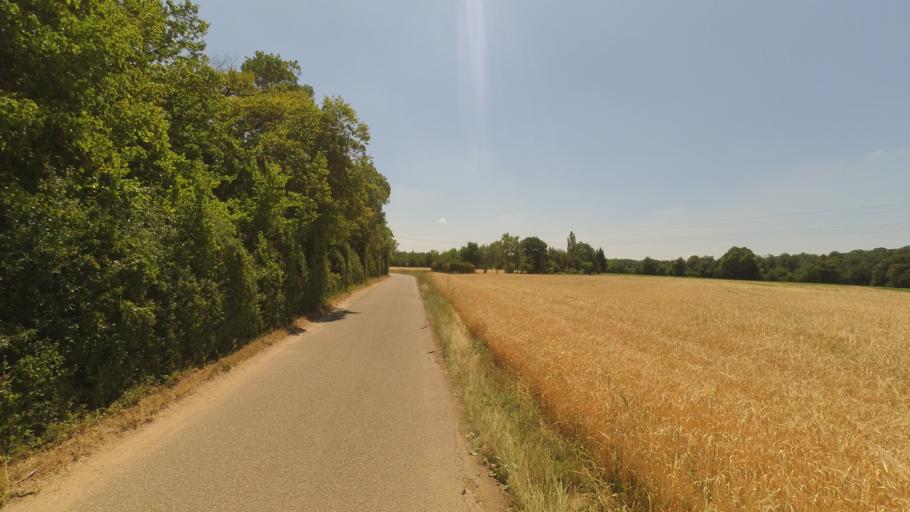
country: DE
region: Baden-Wuerttemberg
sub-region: Karlsruhe Region
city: Schwetzingen
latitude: 49.3810
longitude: 8.5596
